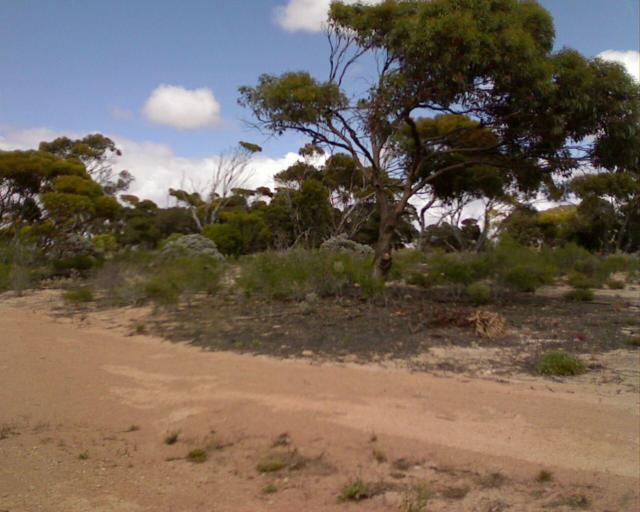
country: AU
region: South Australia
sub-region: Ceduna
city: Ceduna
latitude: -32.0992
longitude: 133.5760
